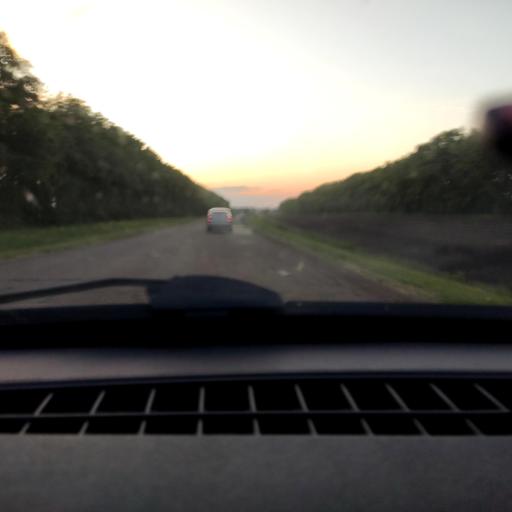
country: RU
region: Bashkortostan
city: Karmaskaly
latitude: 54.3916
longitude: 56.1731
